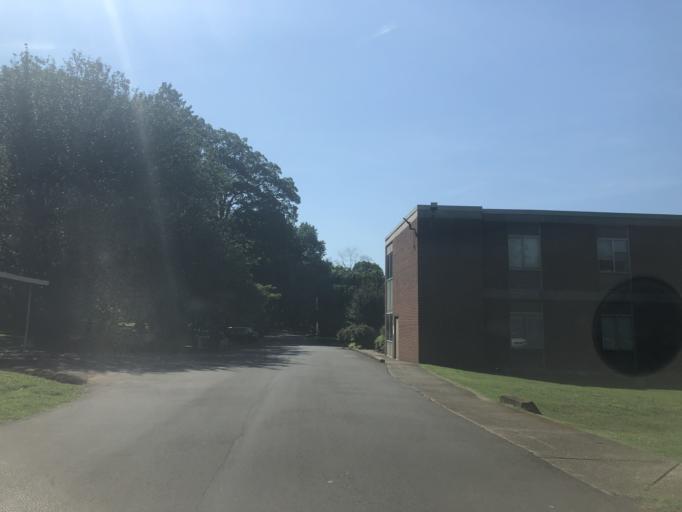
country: US
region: Tennessee
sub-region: Davidson County
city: Lakewood
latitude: 36.2069
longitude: -86.6100
